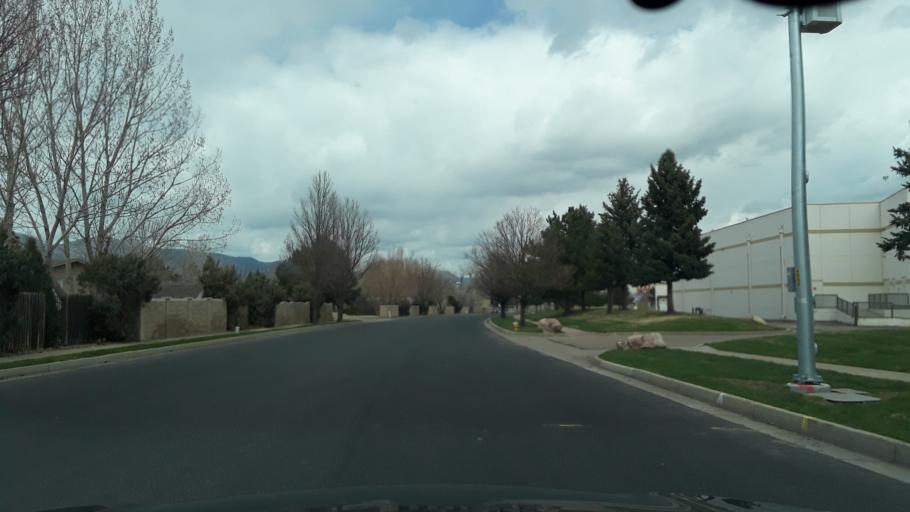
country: US
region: Colorado
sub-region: El Paso County
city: Air Force Academy
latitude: 38.9420
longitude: -104.8027
